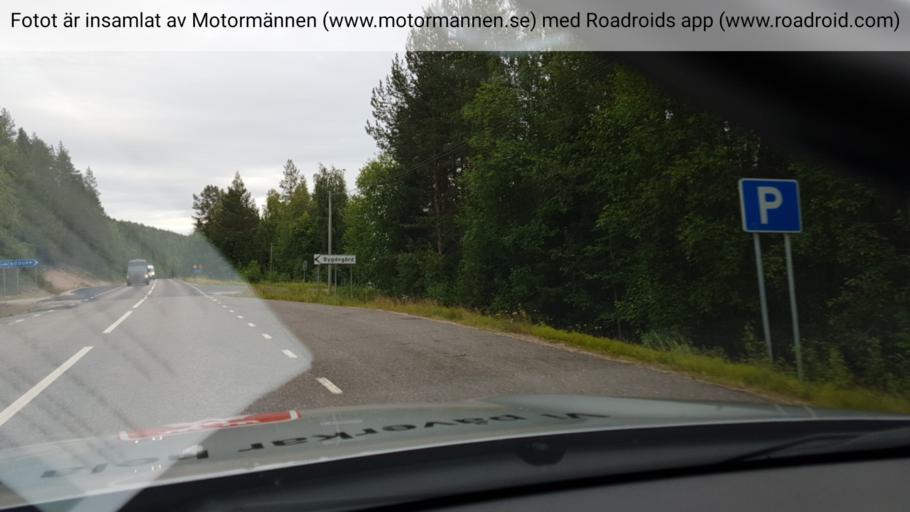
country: SE
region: Norrbotten
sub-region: Overkalix Kommun
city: OEverkalix
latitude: 66.4889
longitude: 22.7786
